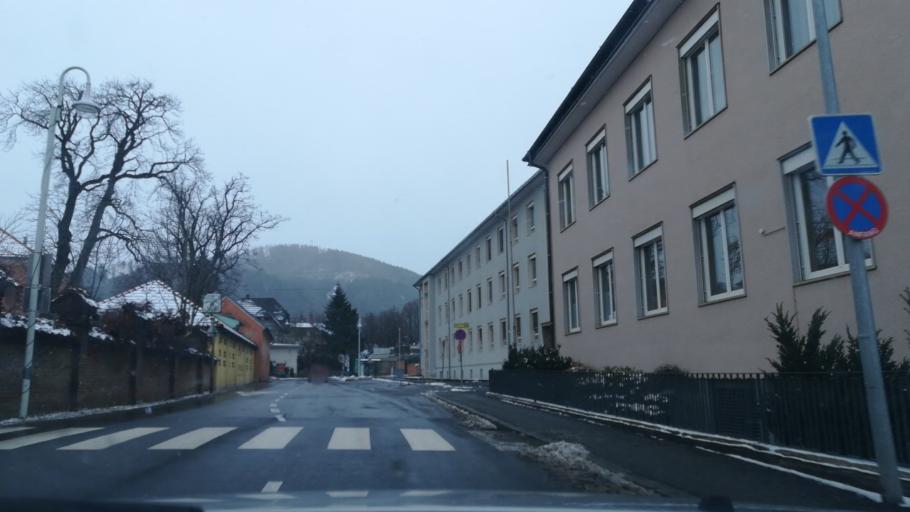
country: AT
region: Styria
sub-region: Politischer Bezirk Murtal
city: Judenburg
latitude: 47.1699
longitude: 14.6555
